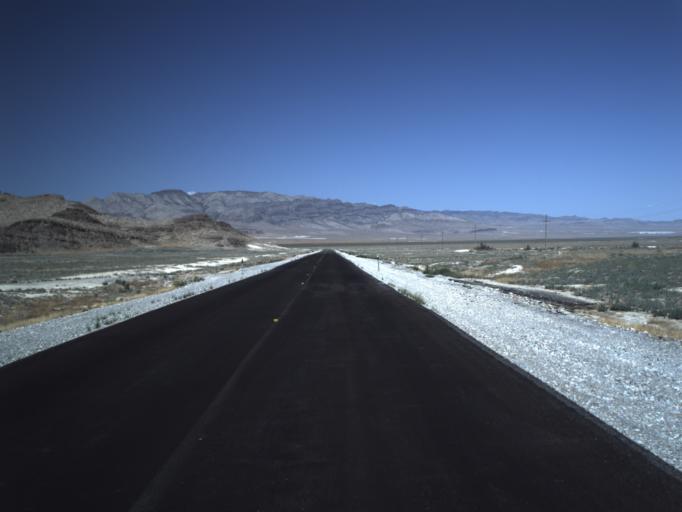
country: US
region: Utah
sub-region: Beaver County
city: Milford
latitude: 39.0582
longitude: -113.4338
